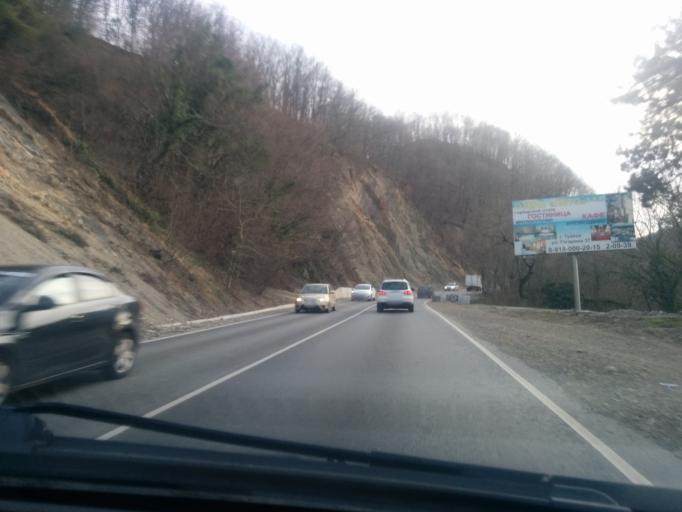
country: RU
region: Krasnodarskiy
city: Agoy
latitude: 44.1351
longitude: 39.0513
